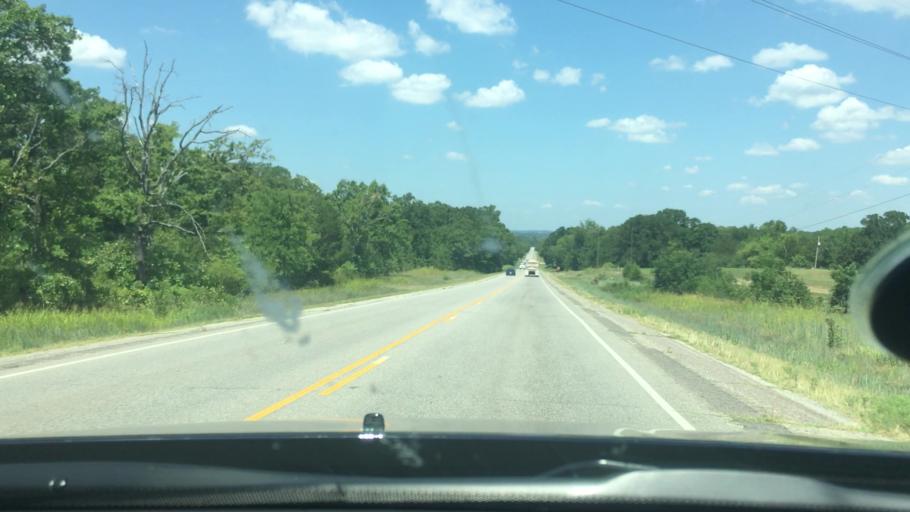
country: US
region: Oklahoma
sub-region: Marshall County
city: Oakland
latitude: 34.1562
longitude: -96.8192
